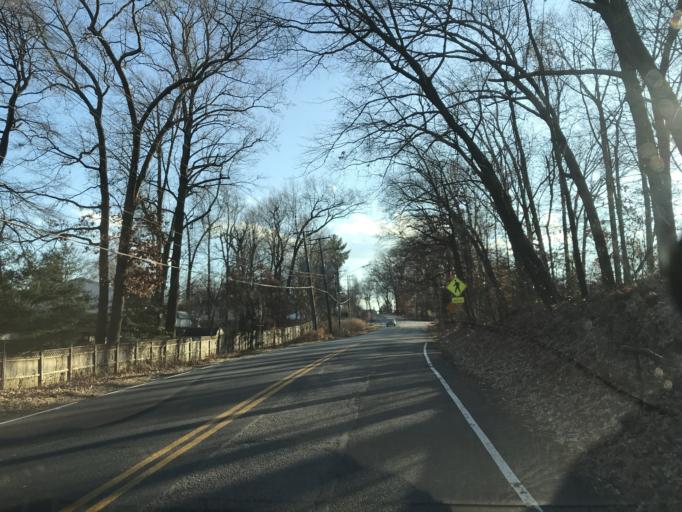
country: US
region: Virginia
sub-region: Fairfax County
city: West Springfield
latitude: 38.7739
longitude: -77.2316
